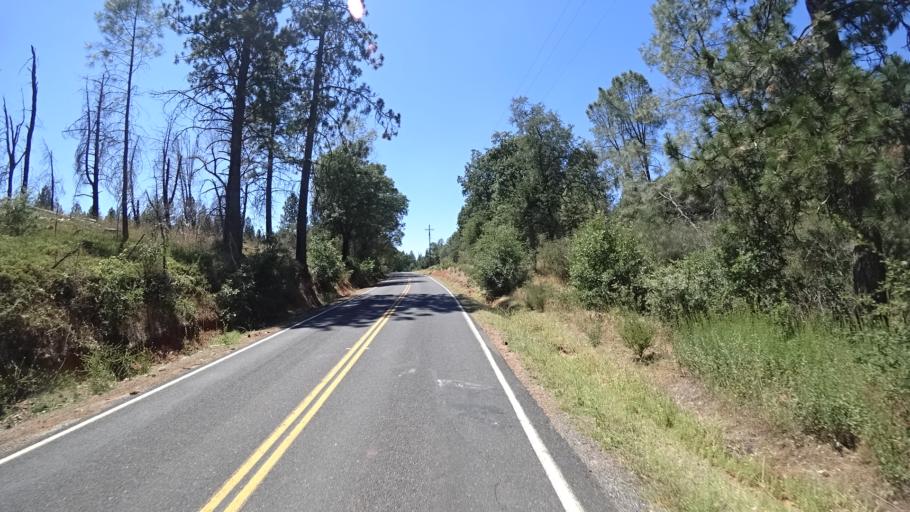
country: US
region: California
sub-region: Calaveras County
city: Mountain Ranch
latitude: 38.3096
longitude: -120.5115
